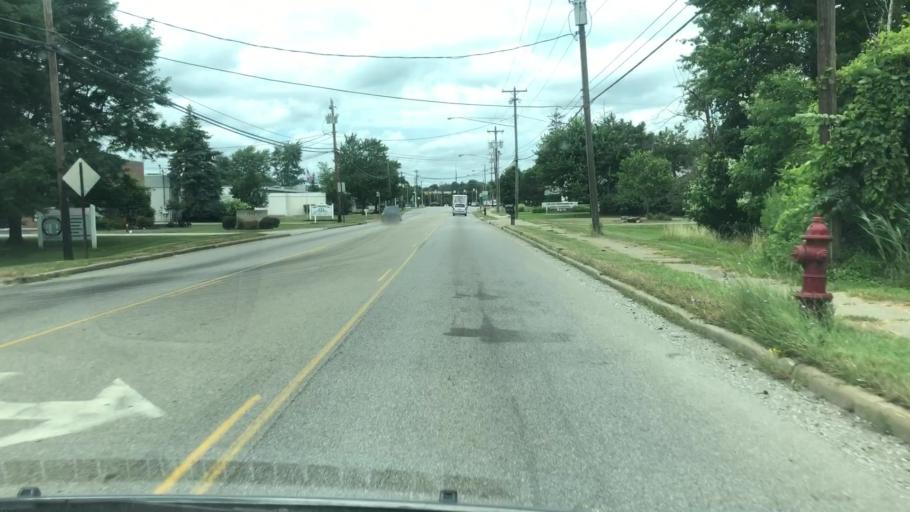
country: US
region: Ohio
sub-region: Summit County
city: Macedonia
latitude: 41.2991
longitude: -81.5108
